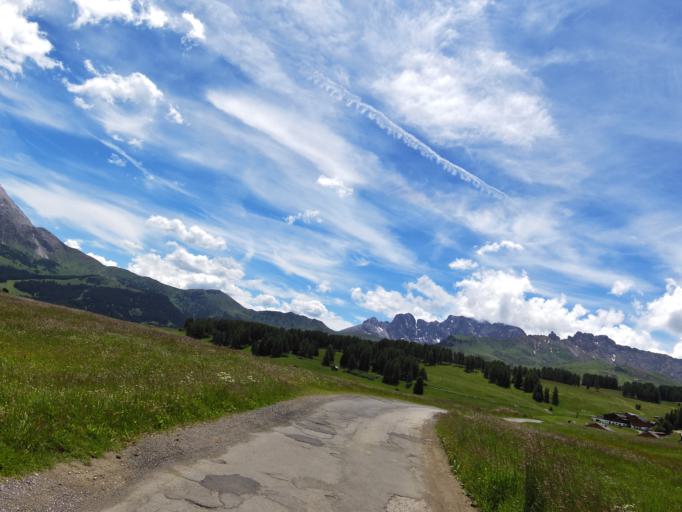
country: IT
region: Trentino-Alto Adige
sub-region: Bolzano
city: Ortisei
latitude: 46.5440
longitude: 11.6472
